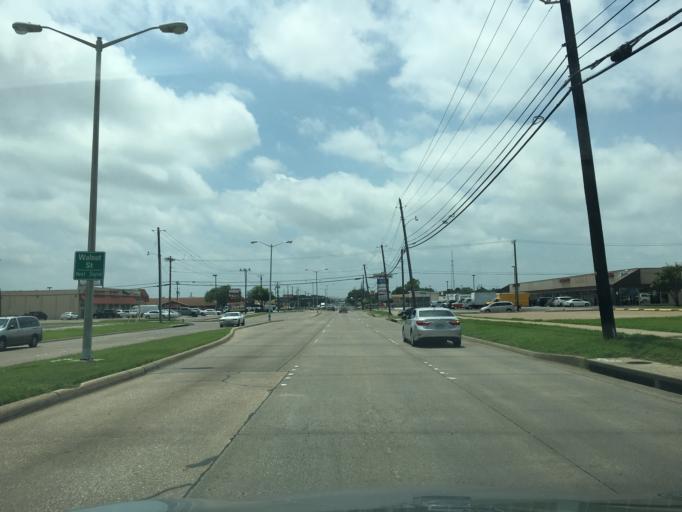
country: US
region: Texas
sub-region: Dallas County
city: Garland
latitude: 32.9202
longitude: -96.6831
